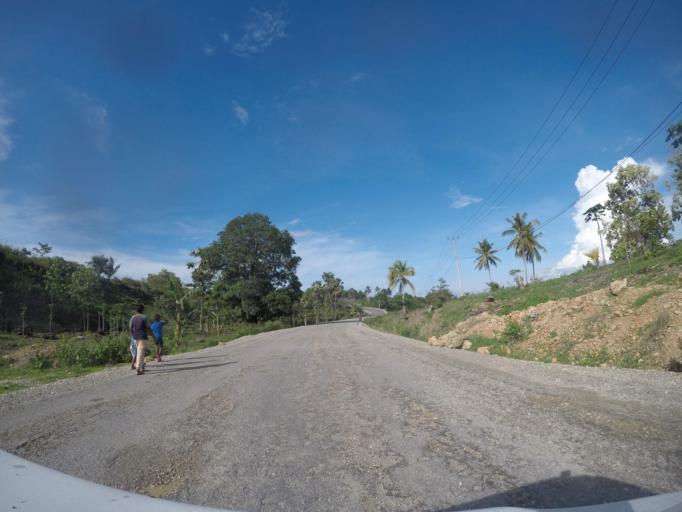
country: TL
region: Baucau
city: Baucau
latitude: -8.5071
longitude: 126.4439
